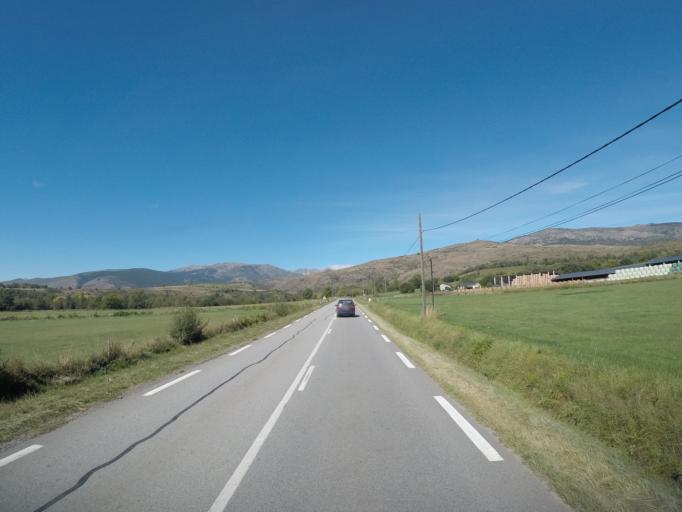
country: FR
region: Languedoc-Roussillon
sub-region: Departement des Pyrenees-Orientales
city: la Guingueta d'Ix
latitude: 42.4568
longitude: 1.9509
